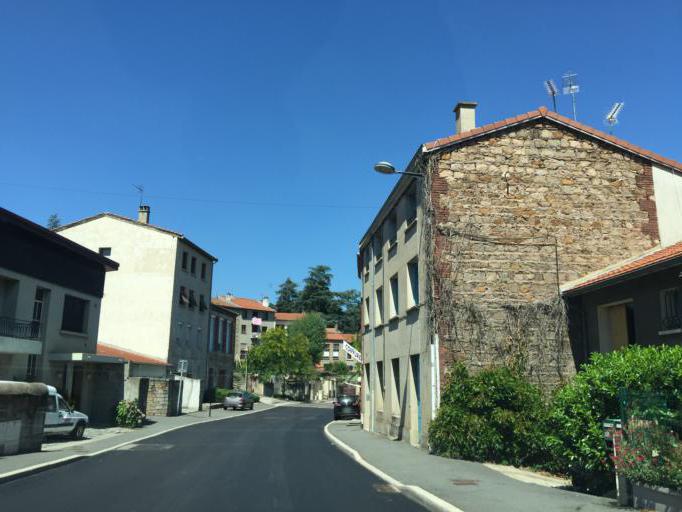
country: FR
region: Rhone-Alpes
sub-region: Departement de la Loire
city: Saint-Jean-Bonnefonds
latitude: 45.4499
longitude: 4.4453
